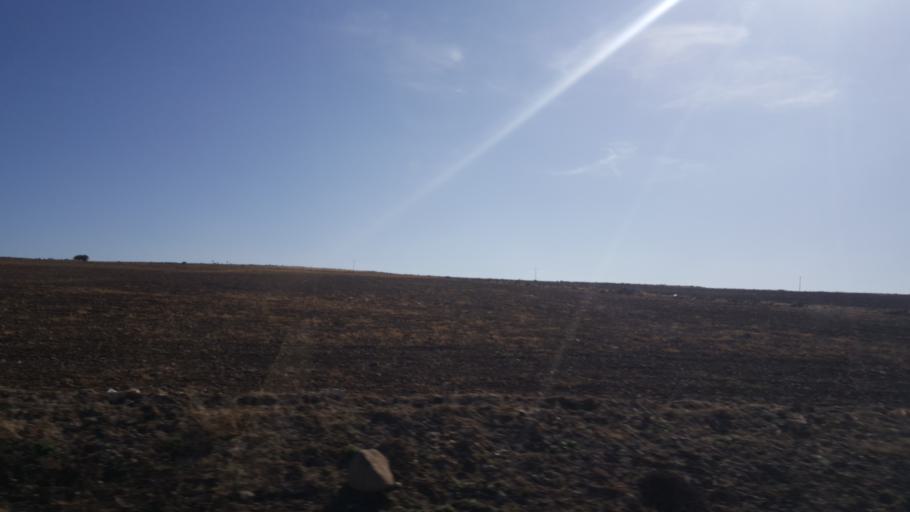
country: TR
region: Ankara
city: Altpinar
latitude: 39.2415
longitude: 32.7274
